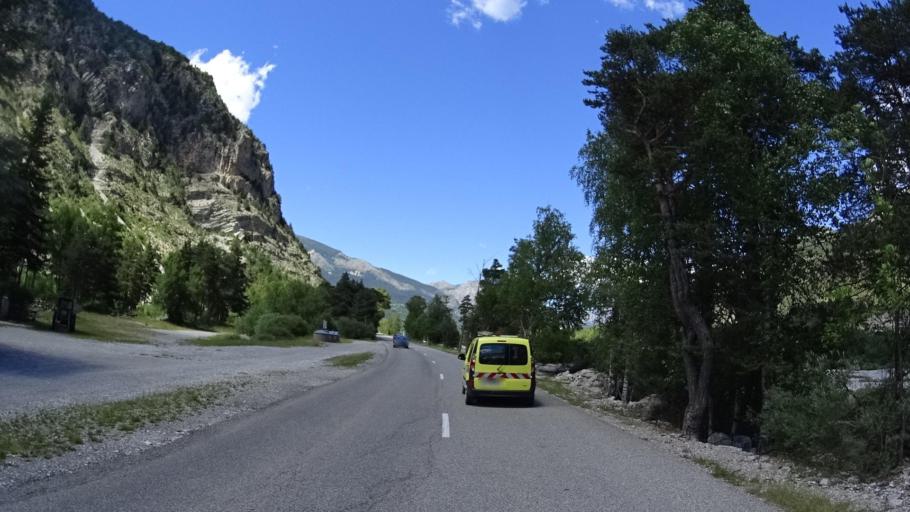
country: FR
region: Provence-Alpes-Cote d'Azur
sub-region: Departement des Alpes-de-Haute-Provence
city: Annot
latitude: 44.1111
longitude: 6.5792
